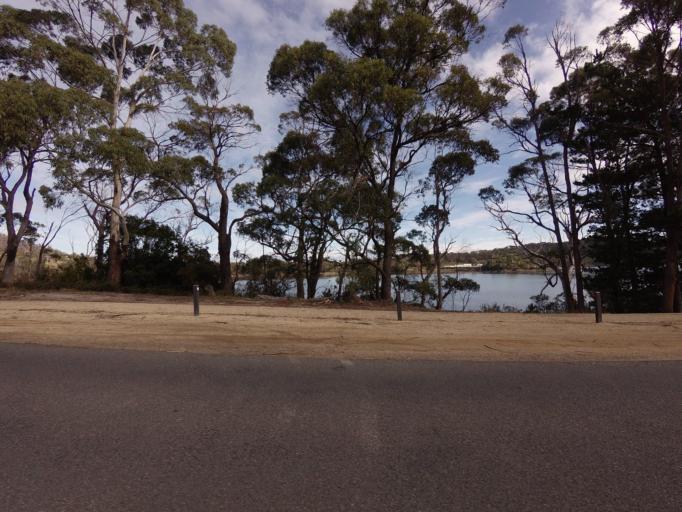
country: AU
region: Tasmania
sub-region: Clarence
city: Sandford
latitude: -43.1056
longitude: 147.7438
